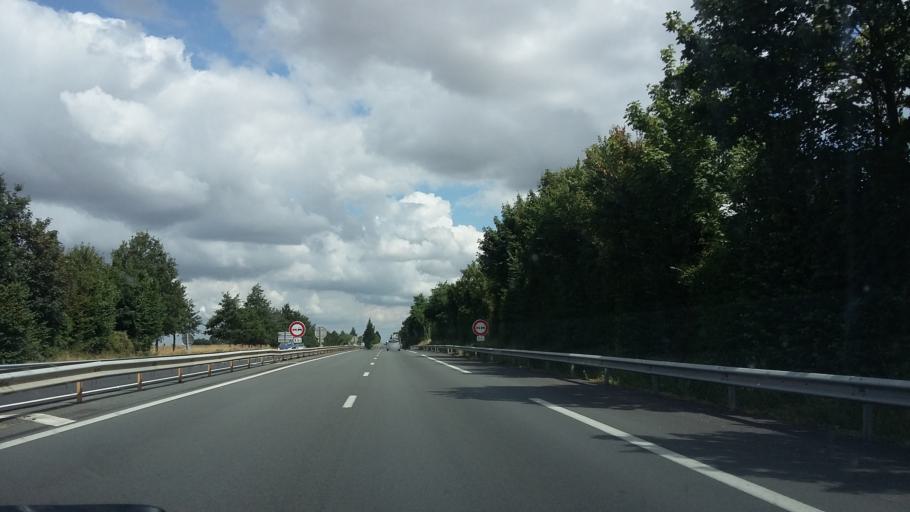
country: FR
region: Poitou-Charentes
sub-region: Departement de la Vienne
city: Couhe
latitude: 46.3202
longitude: 0.1867
